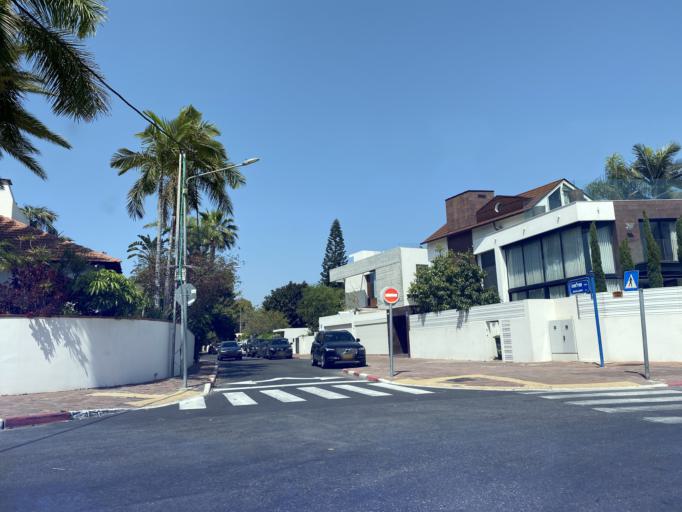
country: IL
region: Tel Aviv
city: Herzliya Pituah
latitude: 32.1730
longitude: 34.8110
